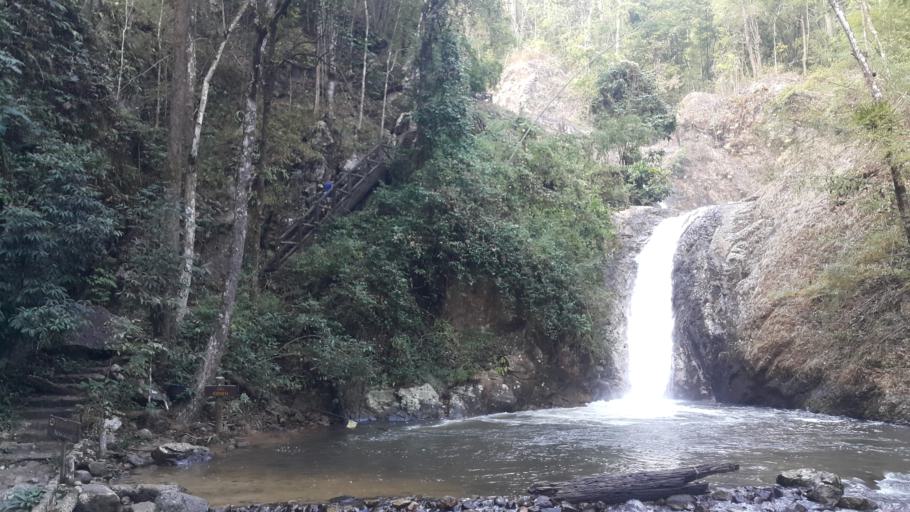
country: TH
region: Lampang
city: Mueang Pan
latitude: 18.8416
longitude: 99.4679
